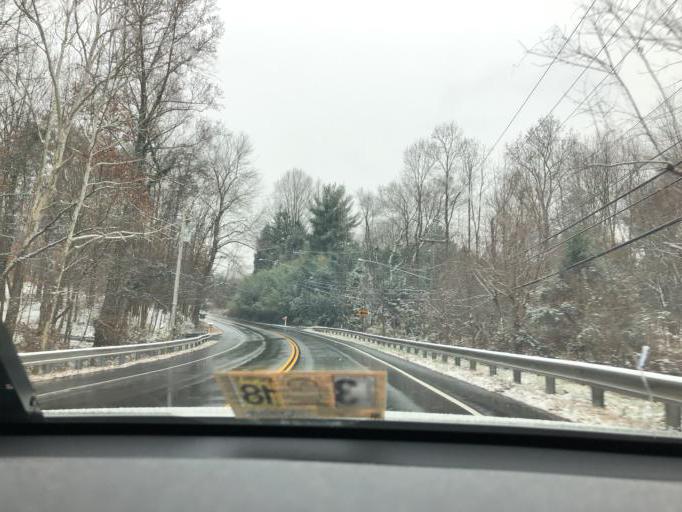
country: US
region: Virginia
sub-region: Fairfax County
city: Oakton
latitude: 38.8980
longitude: -77.3044
